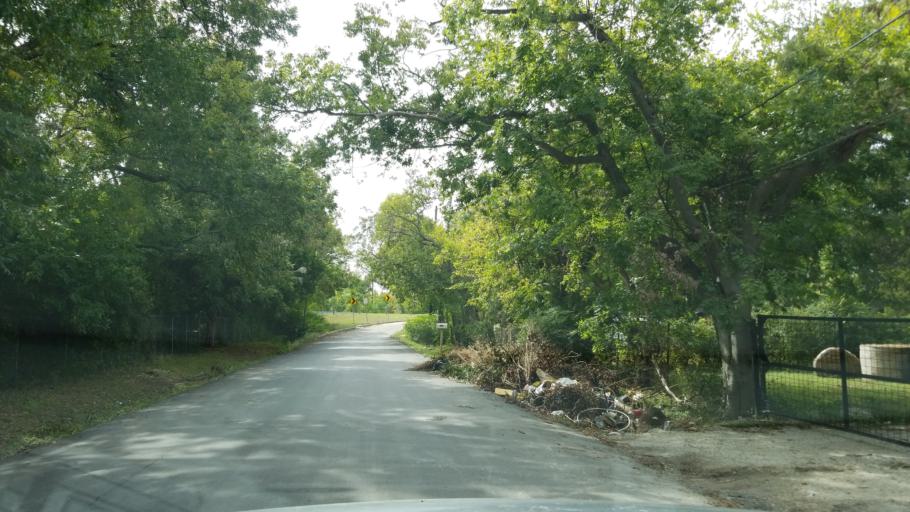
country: US
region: Texas
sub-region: Dallas County
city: Dallas
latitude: 32.7795
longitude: -96.7203
